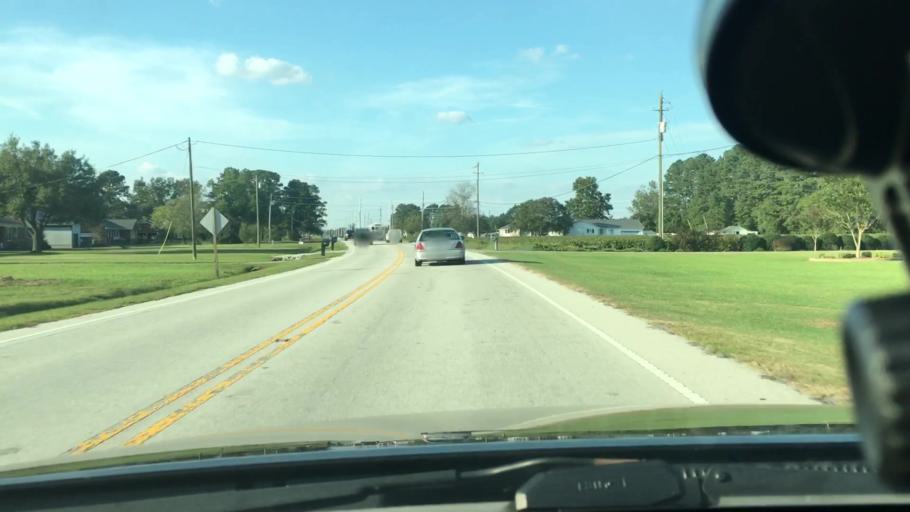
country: US
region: North Carolina
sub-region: Pitt County
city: Windsor
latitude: 35.5261
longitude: -77.3192
